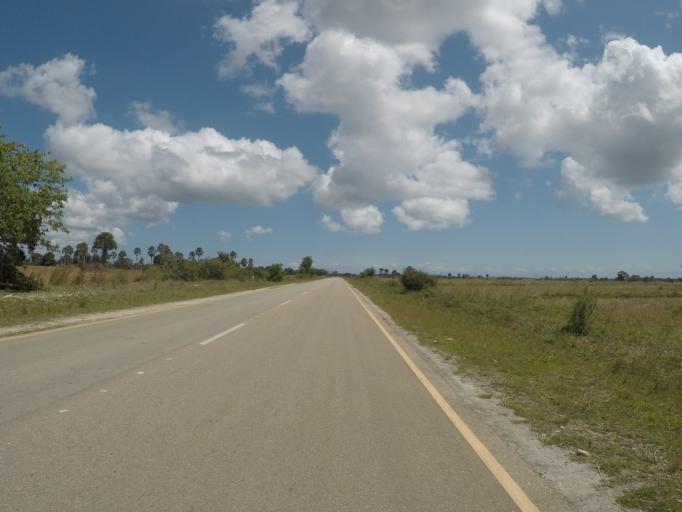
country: TZ
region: Zanzibar Central/South
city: Koani
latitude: -6.2049
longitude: 39.3677
